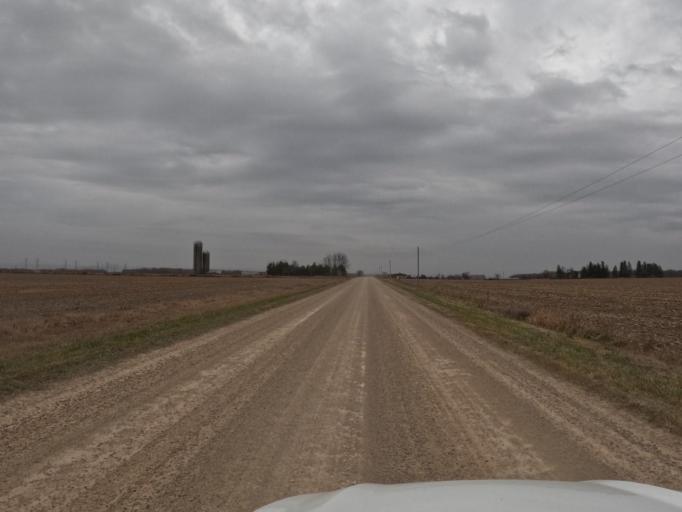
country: CA
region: Ontario
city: Shelburne
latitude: 43.8855
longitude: -80.3590
